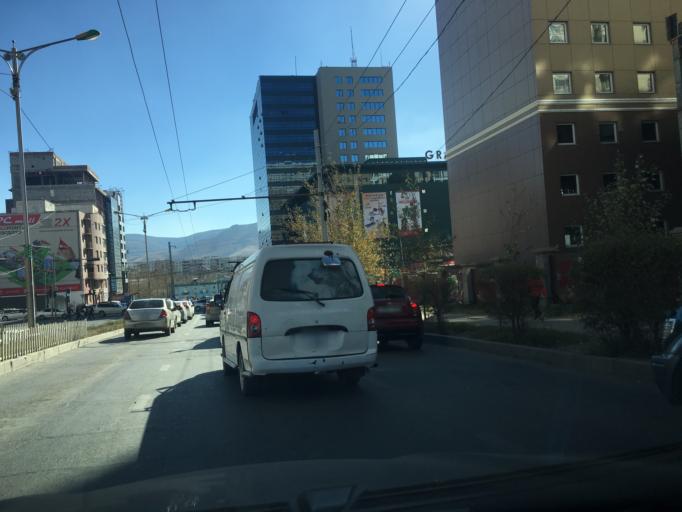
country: MN
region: Ulaanbaatar
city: Ulaanbaatar
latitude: 47.9158
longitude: 106.8910
